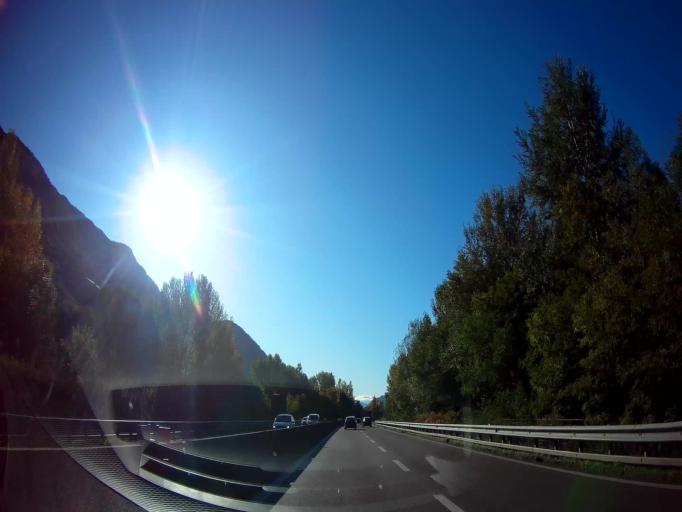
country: IT
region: Trentino-Alto Adige
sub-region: Bolzano
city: Sinigo
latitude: 46.6216
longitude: 11.1827
